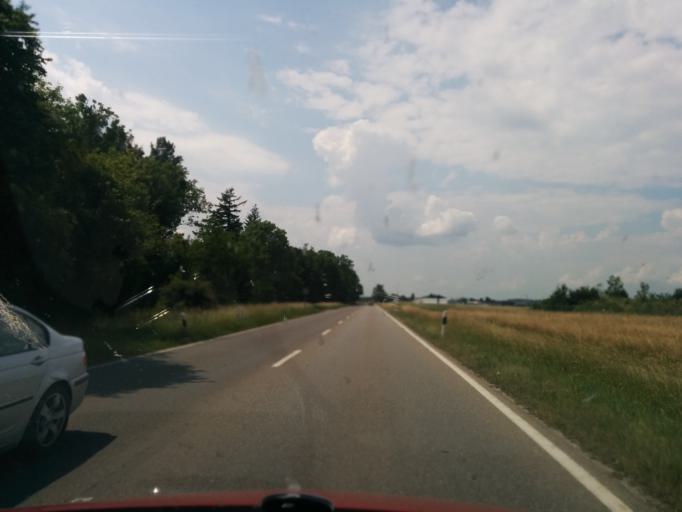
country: DE
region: Bavaria
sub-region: Swabia
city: Bad Worishofen
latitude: 48.0310
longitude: 10.6142
